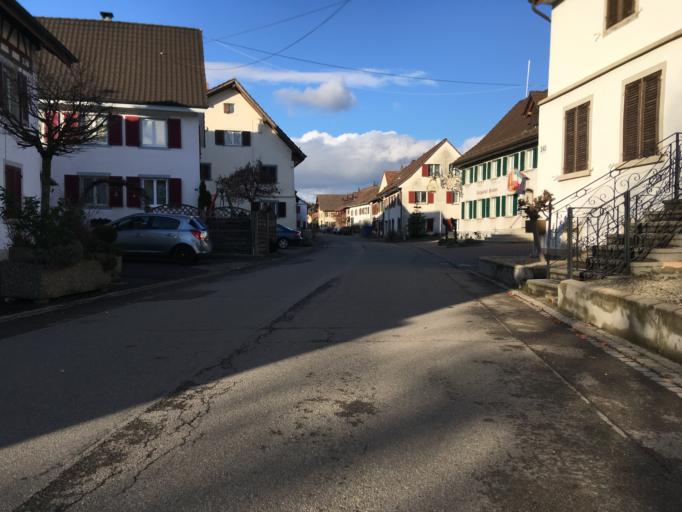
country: CH
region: Schaffhausen
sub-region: Bezirk Stein
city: Ramsen
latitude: 47.7082
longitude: 8.8097
